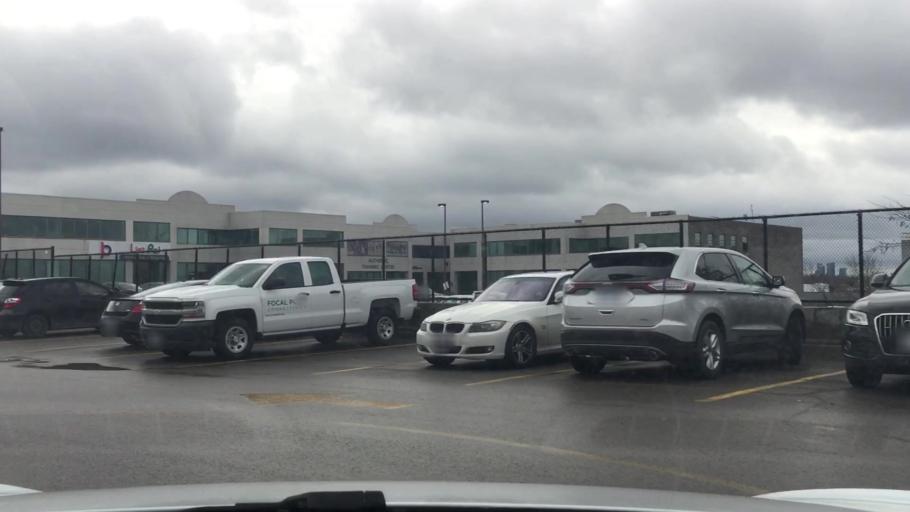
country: CA
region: Ontario
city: Willowdale
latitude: 43.8307
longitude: -79.3543
